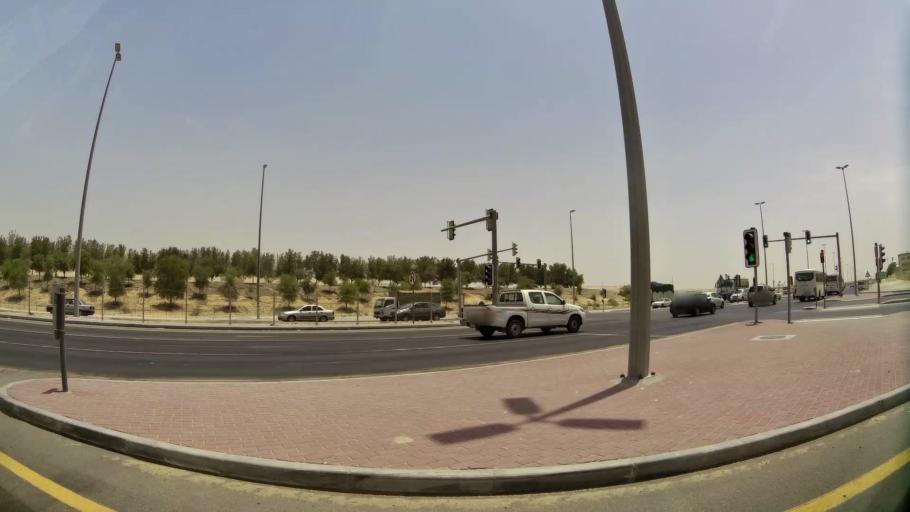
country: AE
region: Ash Shariqah
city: Sharjah
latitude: 25.2742
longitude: 55.4323
